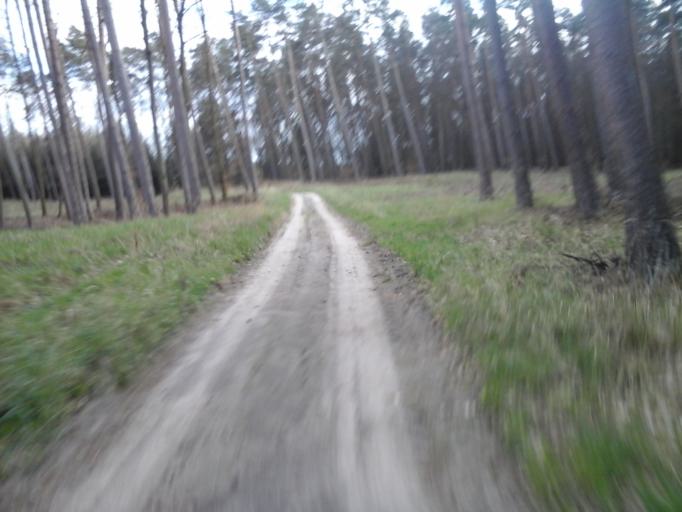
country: PL
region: West Pomeranian Voivodeship
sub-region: Powiat choszczenski
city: Bierzwnik
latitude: 53.0342
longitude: 15.5999
